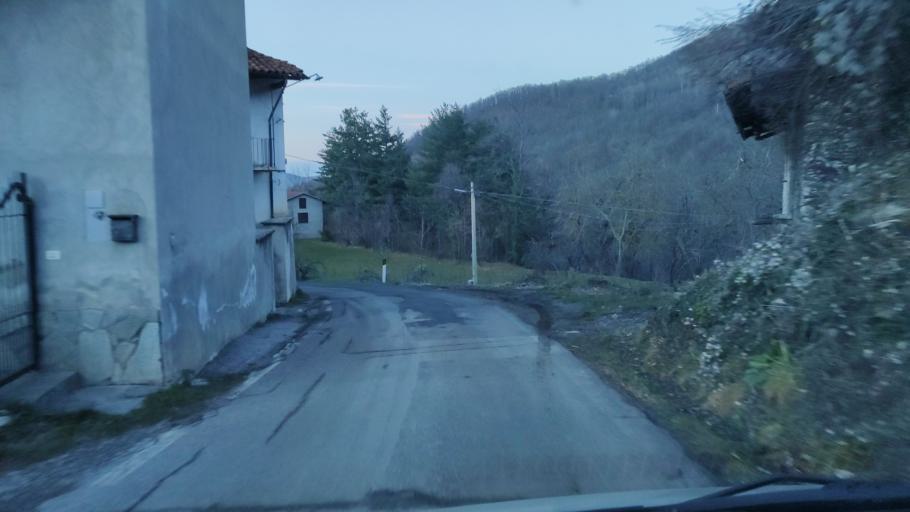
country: IT
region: Piedmont
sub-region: Provincia di Cuneo
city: Lisio
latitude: 44.2922
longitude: 7.9828
